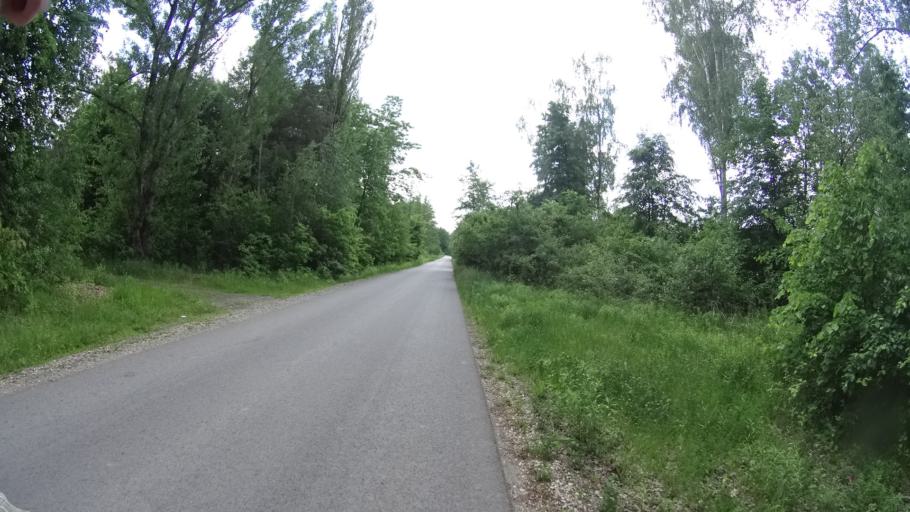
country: PL
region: Masovian Voivodeship
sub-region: Powiat pruszkowski
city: Nadarzyn
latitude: 52.0733
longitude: 20.8186
